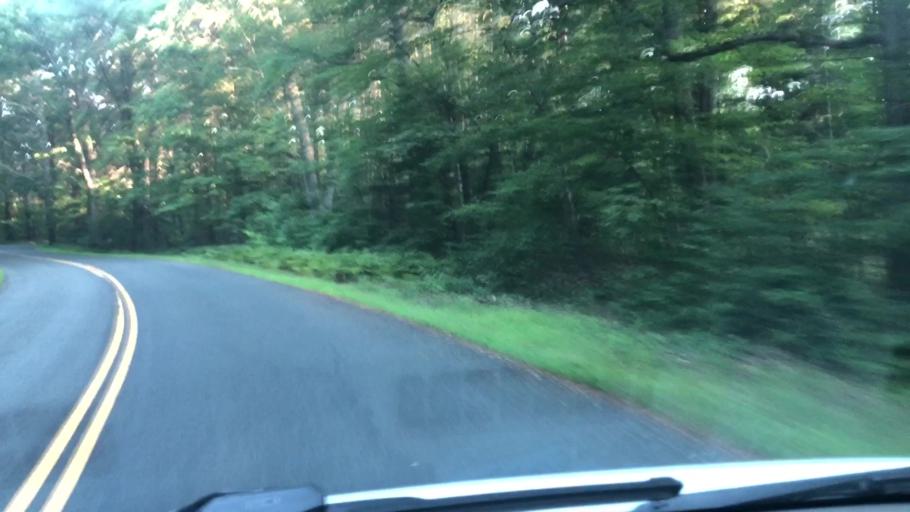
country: US
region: Massachusetts
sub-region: Hampshire County
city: Williamsburg
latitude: 42.3351
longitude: -72.7217
